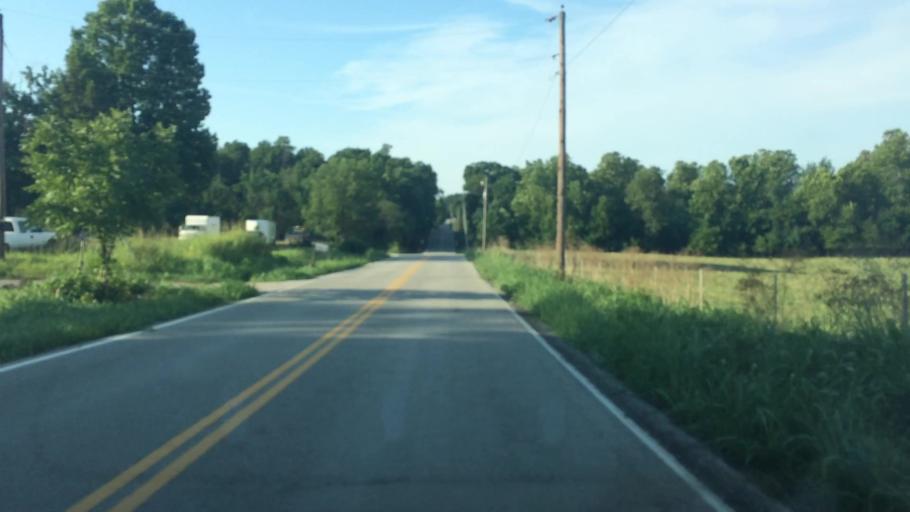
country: US
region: Missouri
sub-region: Greene County
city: Strafford
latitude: 37.2611
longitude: -93.1878
